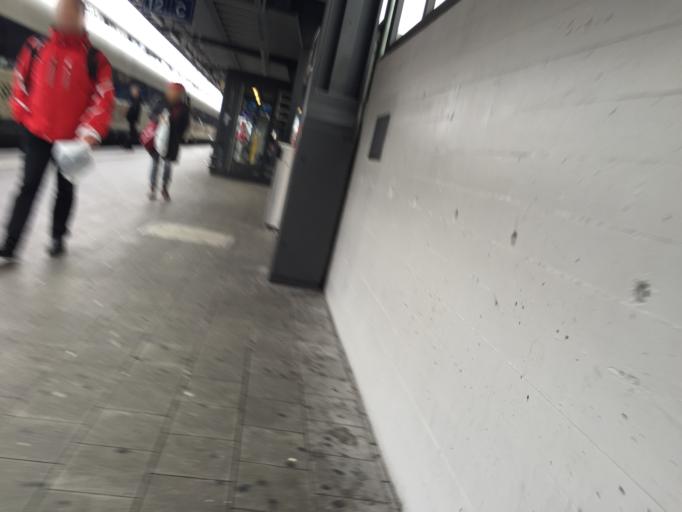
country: CH
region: Solothurn
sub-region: Bezirk Olten
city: Olten
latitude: 47.3519
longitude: 7.9084
